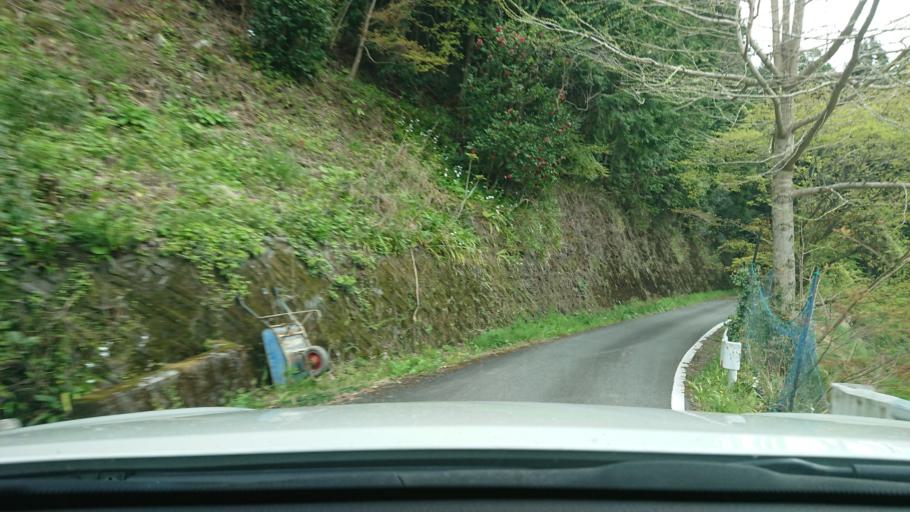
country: JP
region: Tokushima
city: Kamojimacho-jogejima
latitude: 33.8857
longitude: 134.3799
